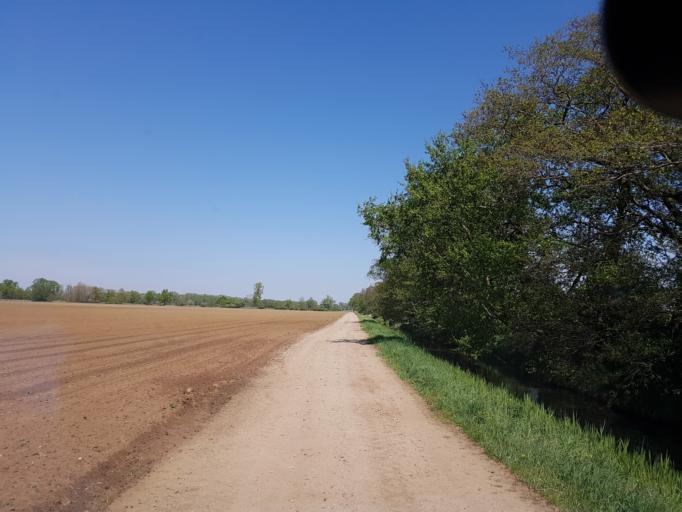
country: DE
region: Brandenburg
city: Schonewalde
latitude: 51.6775
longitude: 13.5832
